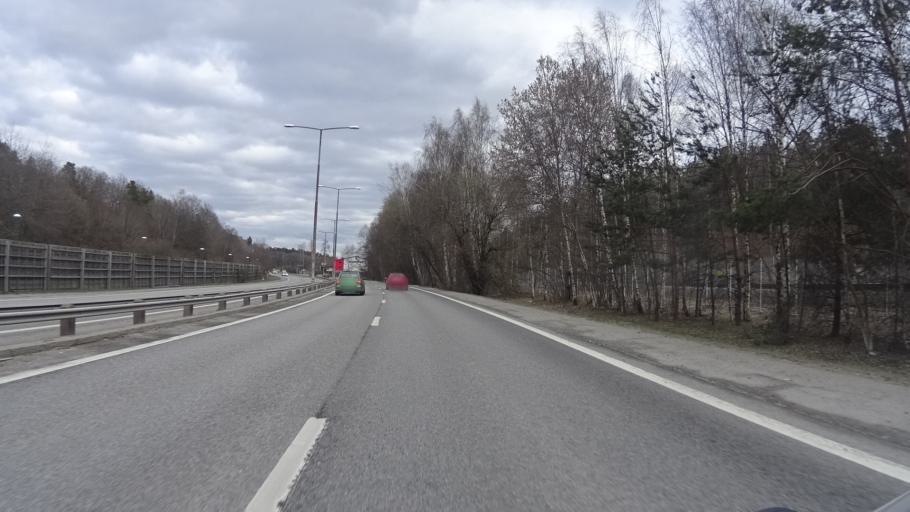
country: SE
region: Stockholm
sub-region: Stockholms Kommun
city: Arsta
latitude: 59.2638
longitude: 18.0264
